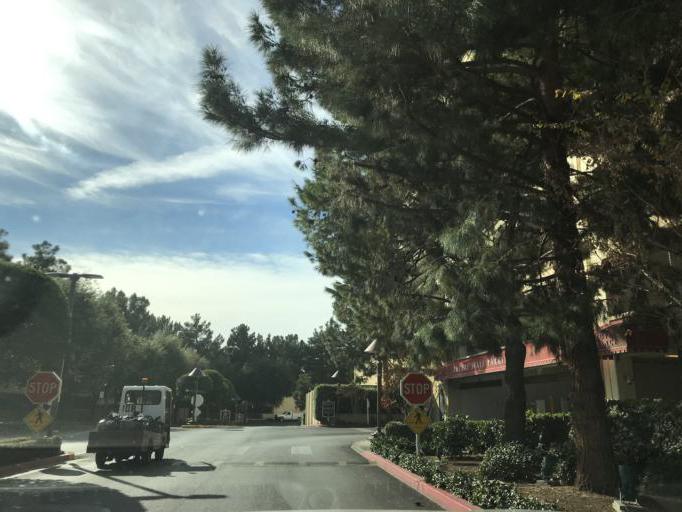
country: US
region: Nevada
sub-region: Clark County
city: Paradise
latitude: 36.1286
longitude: -115.1624
